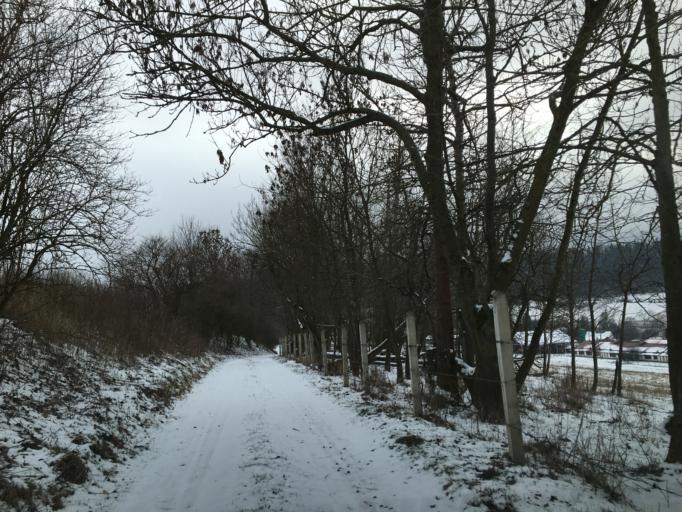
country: PL
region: Lower Silesian Voivodeship
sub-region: Powiat walbrzyski
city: Mieroszow
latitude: 50.7054
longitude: 16.1411
